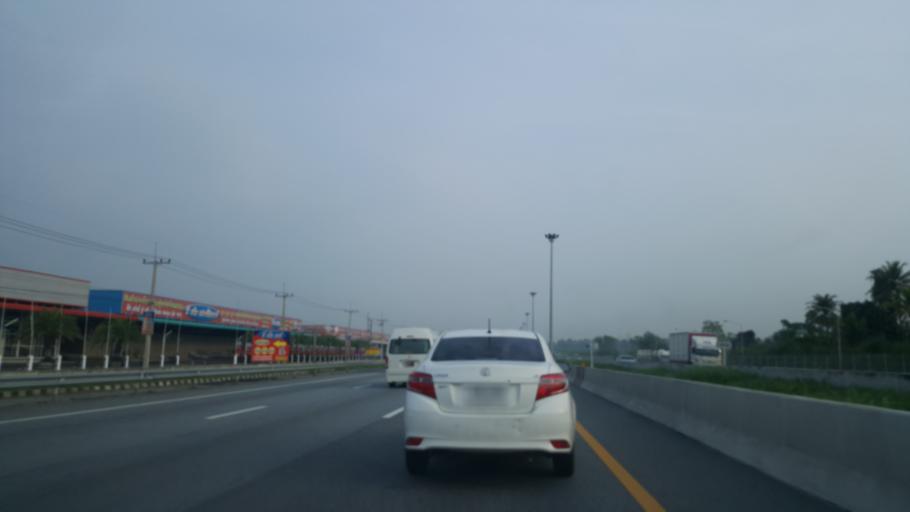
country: TH
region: Chon Buri
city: Ban Talat Bueng
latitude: 13.0220
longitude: 100.9962
